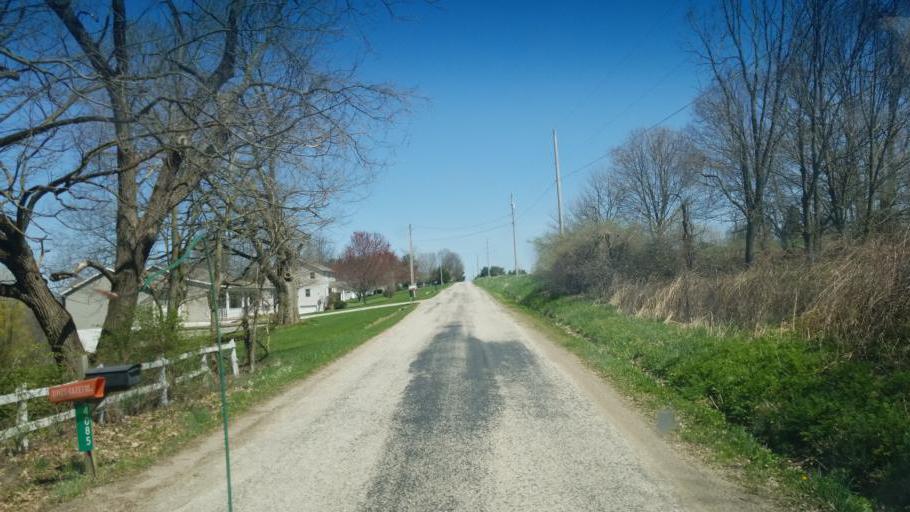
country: US
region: Ohio
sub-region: Ashland County
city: Ashland
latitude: 40.8669
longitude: -82.4161
